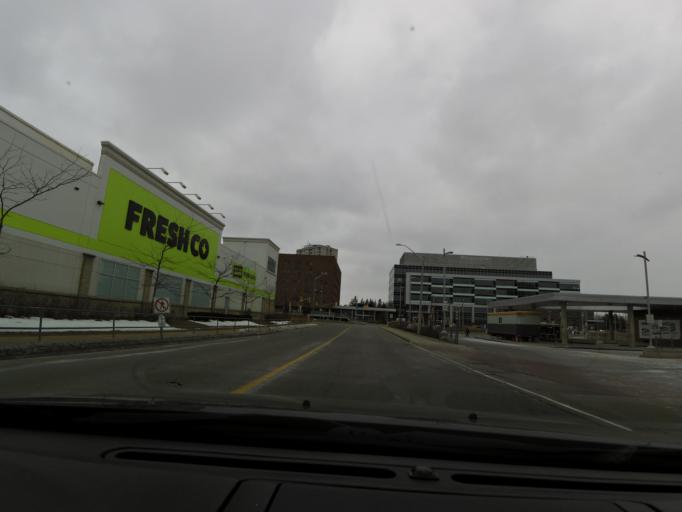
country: CA
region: Ontario
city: Brampton
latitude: 43.7183
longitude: -79.7208
